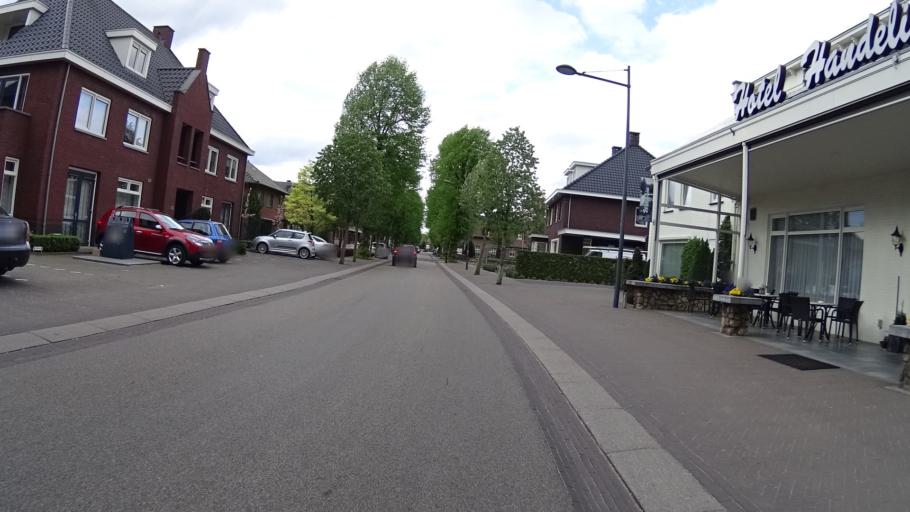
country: NL
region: North Brabant
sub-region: Gemeente Boekel
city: Boekel
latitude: 51.5801
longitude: 5.7135
